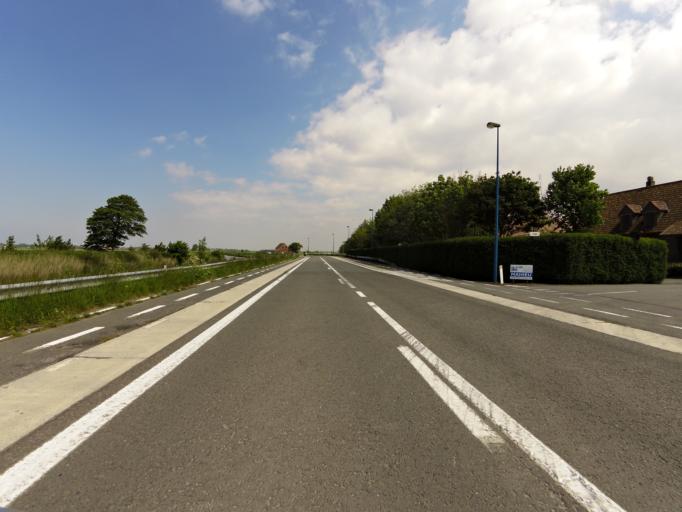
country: BE
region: Flanders
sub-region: Provincie West-Vlaanderen
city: Nieuwpoort
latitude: 51.1113
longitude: 2.7247
